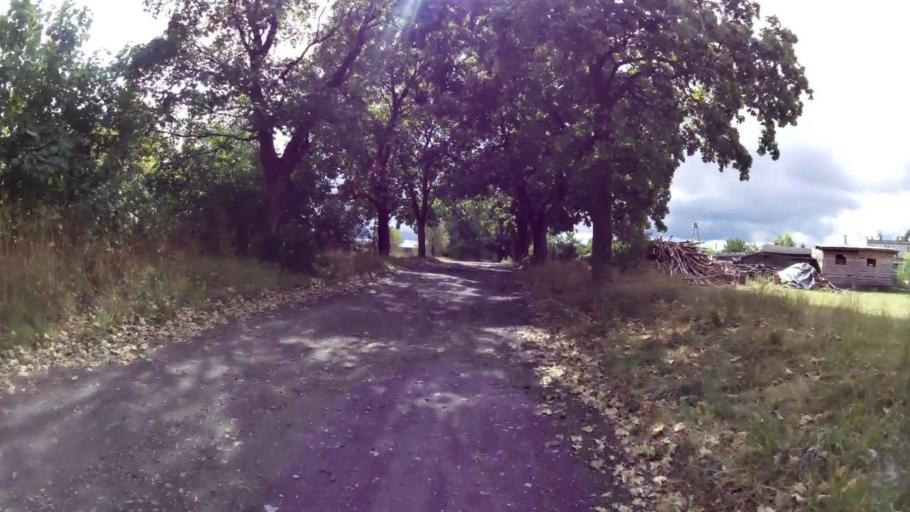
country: PL
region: West Pomeranian Voivodeship
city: Trzcinsko Zdroj
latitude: 52.8808
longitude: 14.7110
